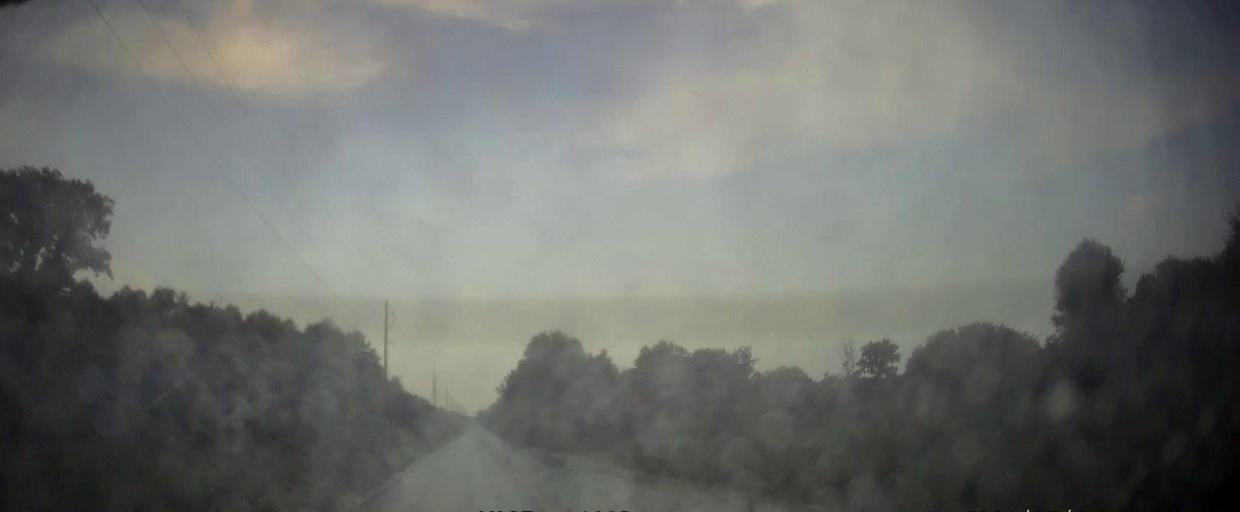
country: US
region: Georgia
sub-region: Dodge County
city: Chester
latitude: 32.5646
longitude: -83.1694
